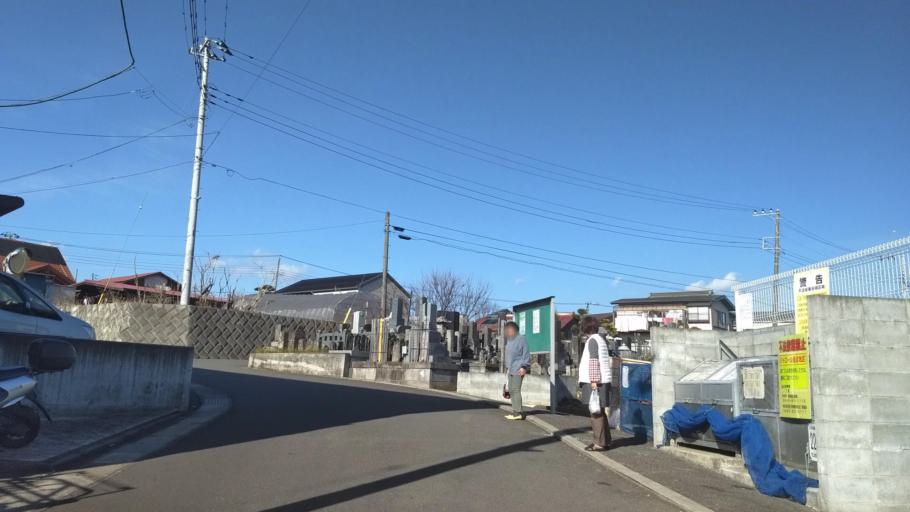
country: JP
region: Kanagawa
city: Hadano
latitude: 35.3423
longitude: 139.2342
